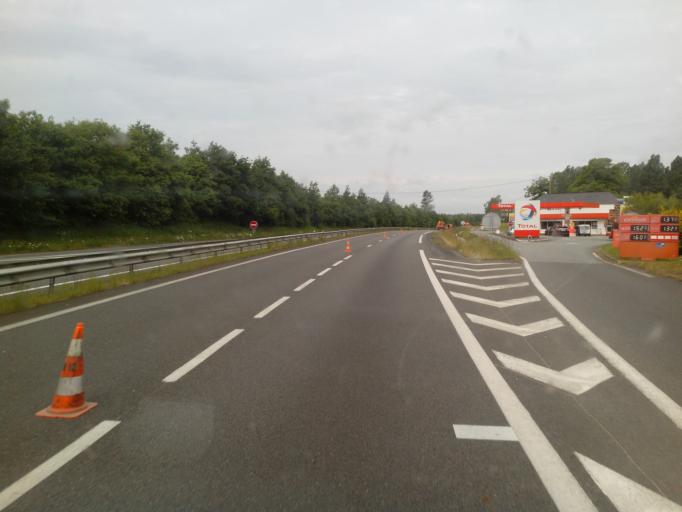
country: FR
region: Brittany
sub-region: Departement des Cotes-d'Armor
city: Caulnes
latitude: 48.2724
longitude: -2.1740
